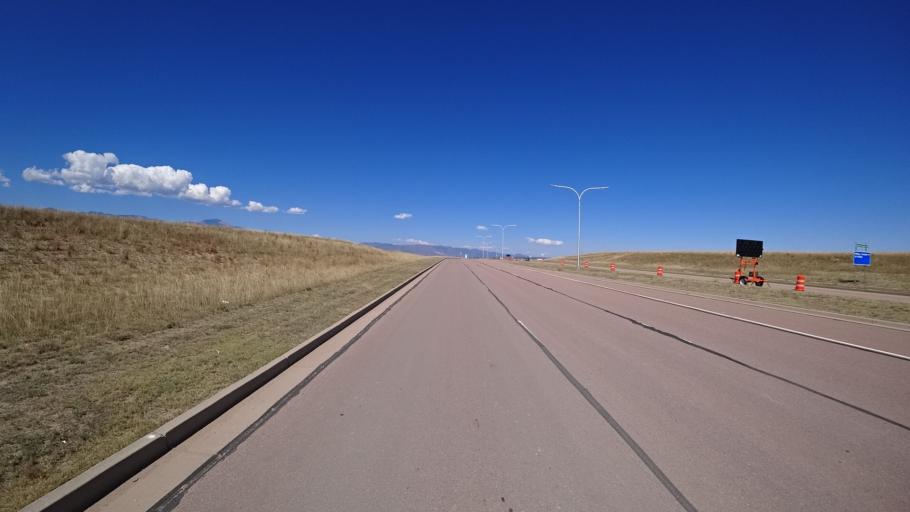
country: US
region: Colorado
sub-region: El Paso County
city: Security-Widefield
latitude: 38.7729
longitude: -104.7018
